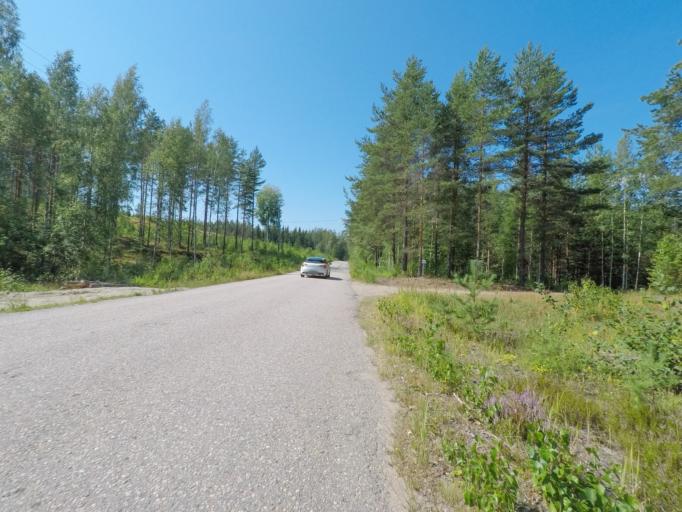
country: FI
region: Southern Savonia
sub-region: Mikkeli
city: Puumala
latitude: 61.4226
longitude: 28.1468
